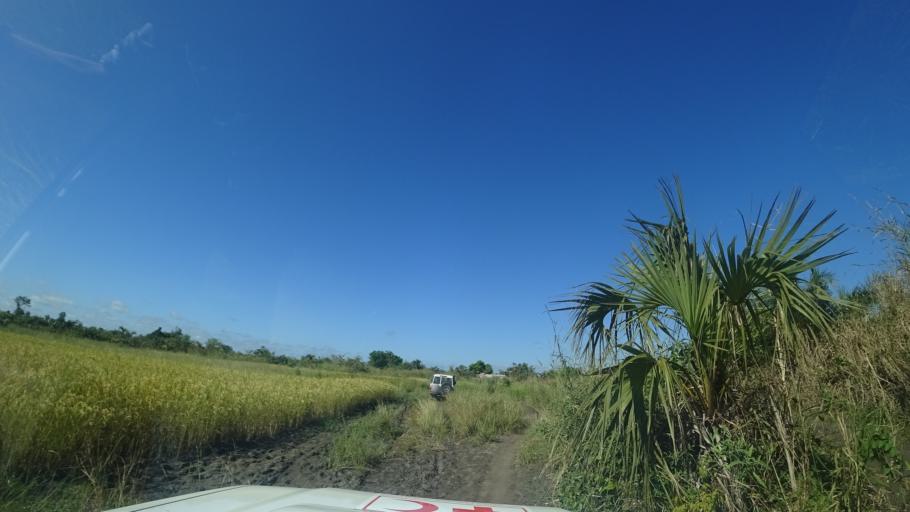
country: MZ
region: Sofala
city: Dondo
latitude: -19.3955
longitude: 34.5934
